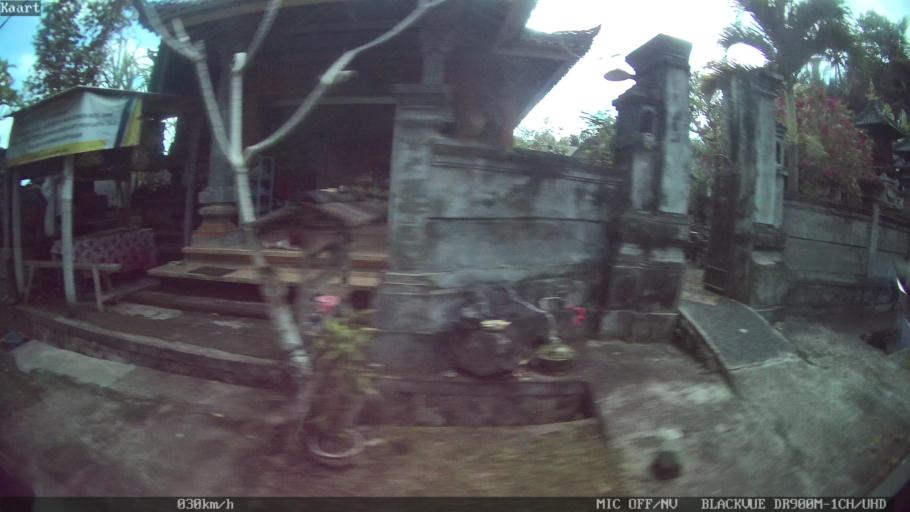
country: ID
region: Bali
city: Banjar Pesalakan
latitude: -8.5131
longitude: 115.3059
